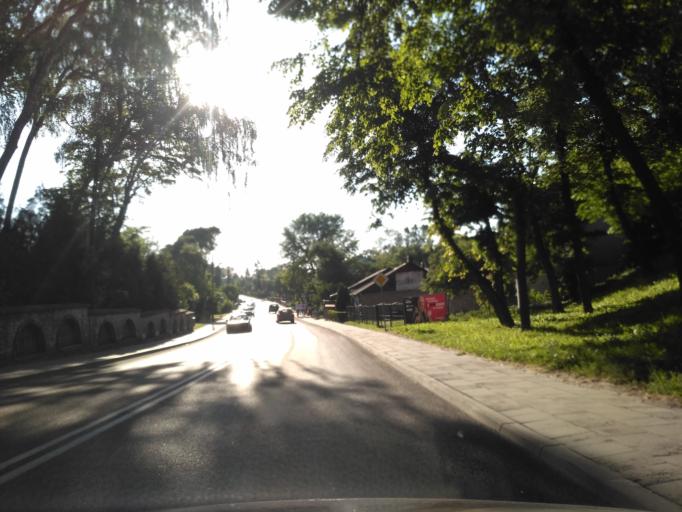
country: PL
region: Lublin Voivodeship
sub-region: Powiat lubelski
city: Bychawa
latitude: 51.0167
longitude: 22.5309
